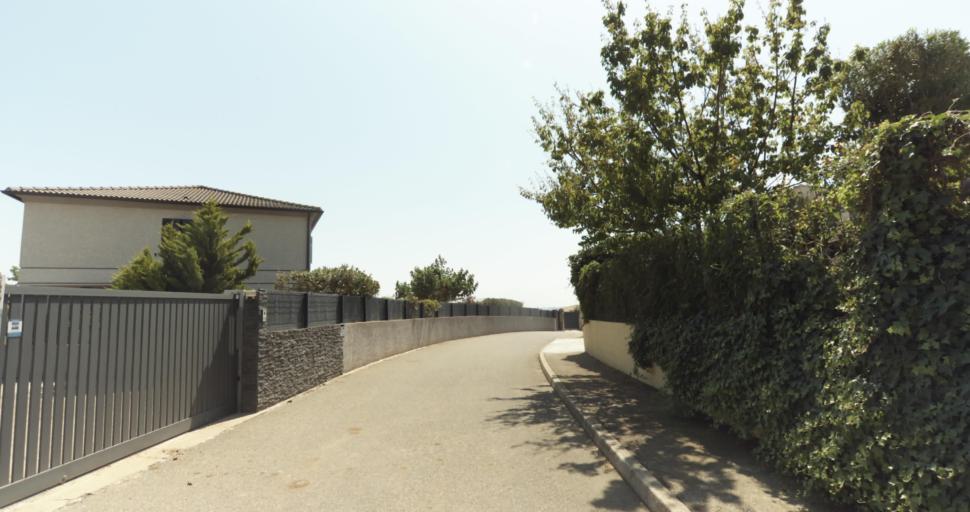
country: FR
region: Corsica
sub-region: Departement de la Haute-Corse
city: Biguglia
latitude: 42.6054
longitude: 9.4283
